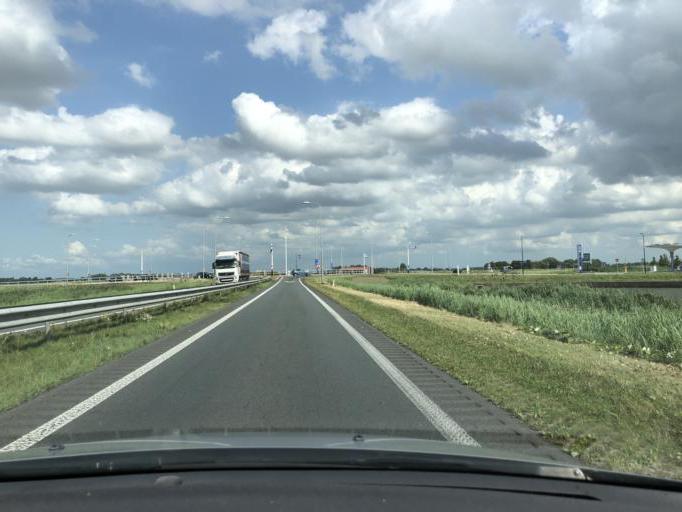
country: NL
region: Flevoland
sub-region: Gemeente Dronten
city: Dronten
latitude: 52.5509
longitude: 5.6923
